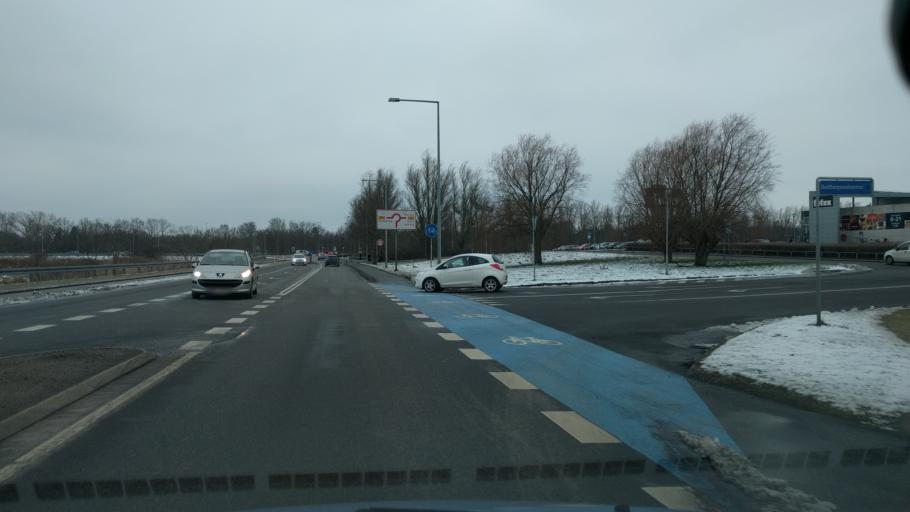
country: DK
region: Zealand
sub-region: Guldborgsund Kommune
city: Nykobing Falster
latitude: 54.7596
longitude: 11.8559
